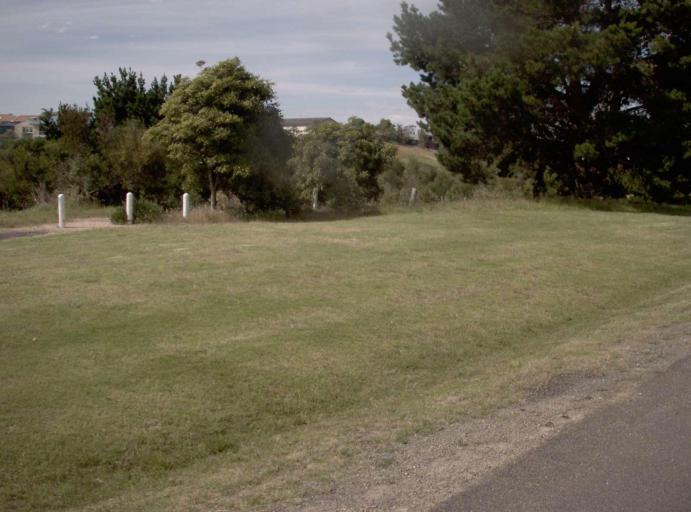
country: AU
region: Victoria
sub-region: East Gippsland
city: Lakes Entrance
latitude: -37.8681
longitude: 148.0150
